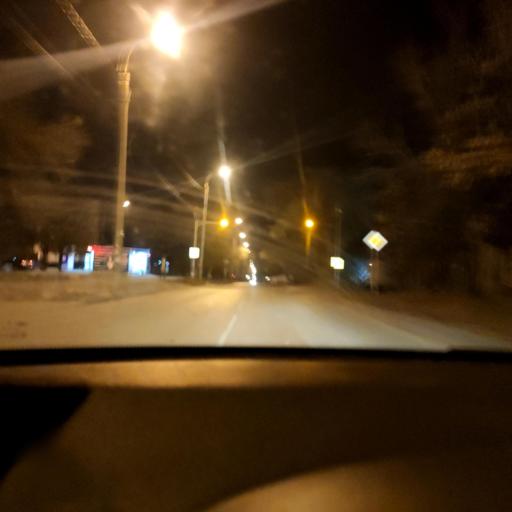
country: RU
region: Samara
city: Samara
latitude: 53.1872
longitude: 50.1834
